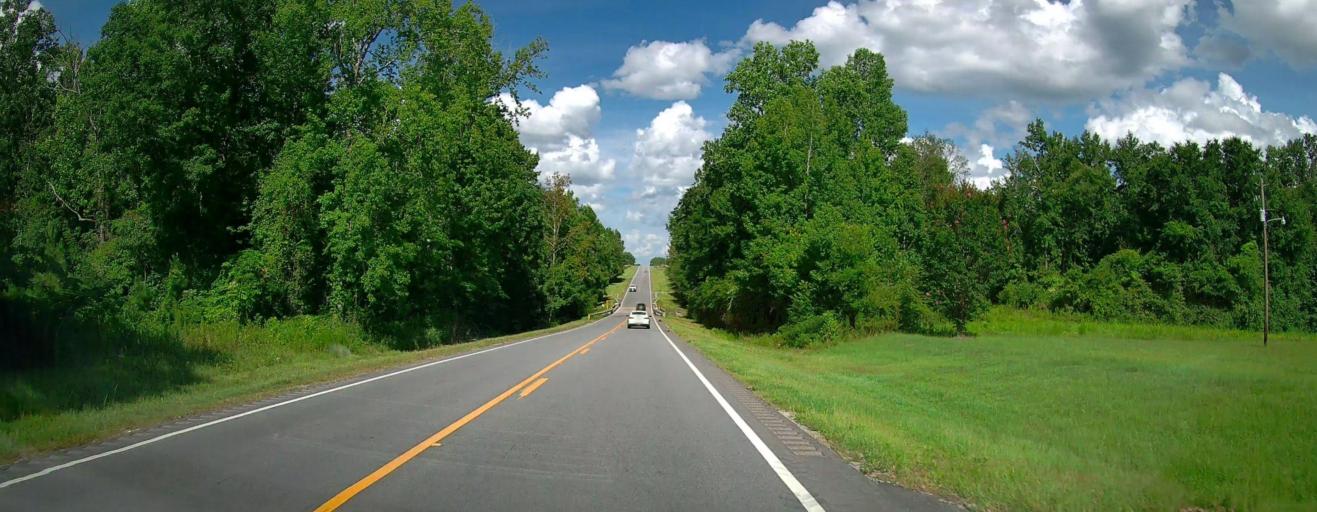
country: US
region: Alabama
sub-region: Lee County
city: Auburn
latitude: 32.4343
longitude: -85.4157
